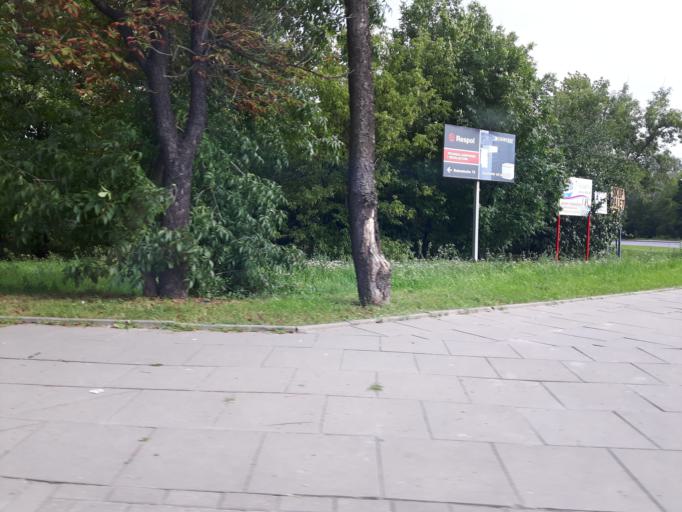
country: PL
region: Masovian Voivodeship
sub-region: Warszawa
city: Praga Poludnie
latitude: 52.2678
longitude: 21.0733
